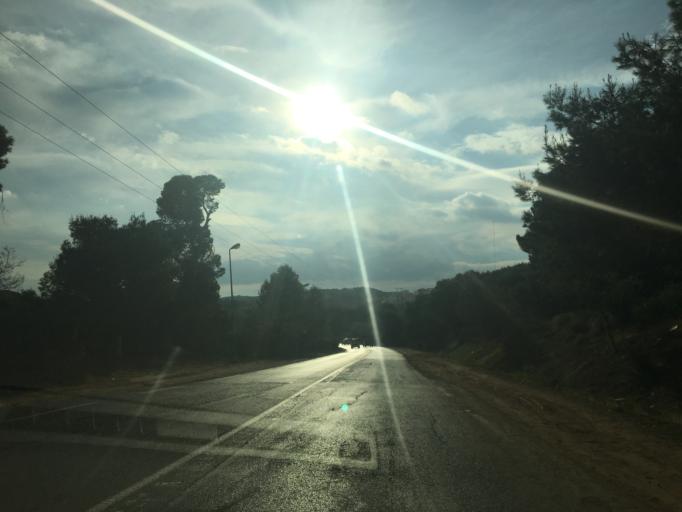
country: DZ
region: Tipaza
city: Tipasa
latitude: 36.5903
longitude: 2.4716
